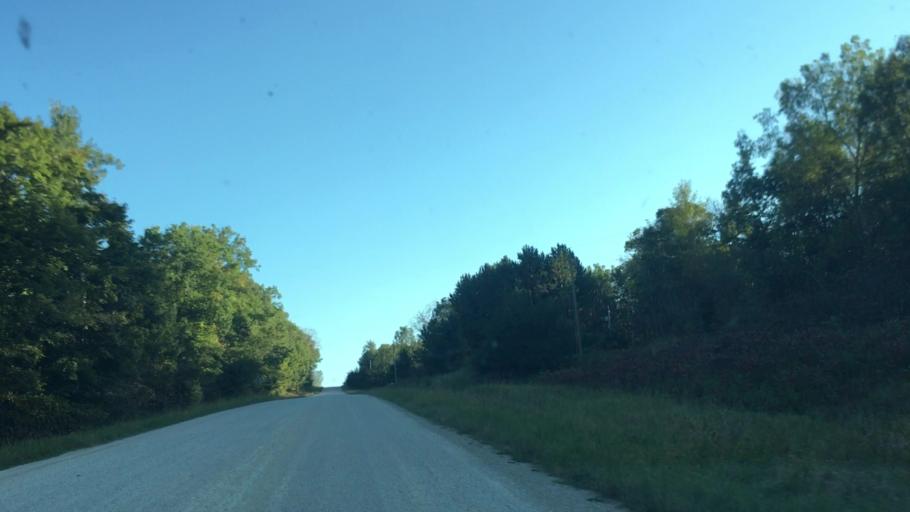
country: US
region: Minnesota
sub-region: Fillmore County
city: Preston
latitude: 43.7808
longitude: -92.0294
